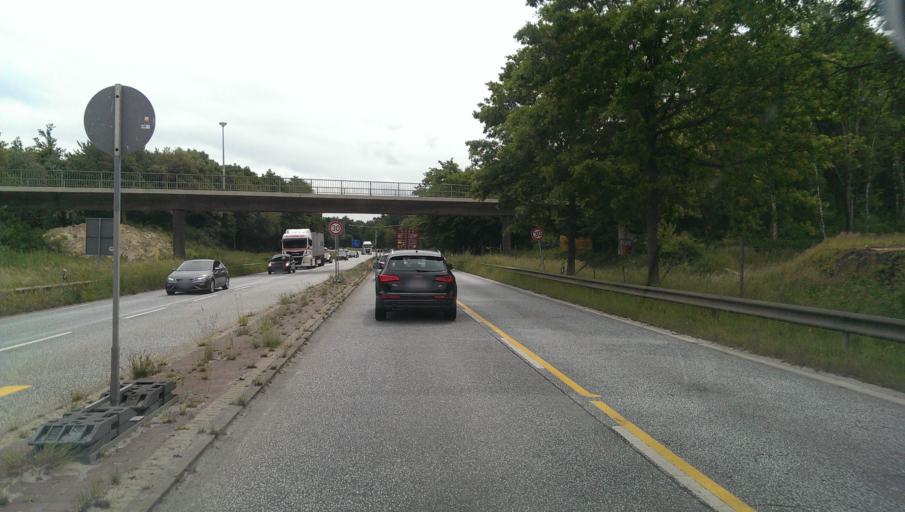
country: DE
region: Lower Saxony
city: Langen
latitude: 53.5831
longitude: 8.6134
